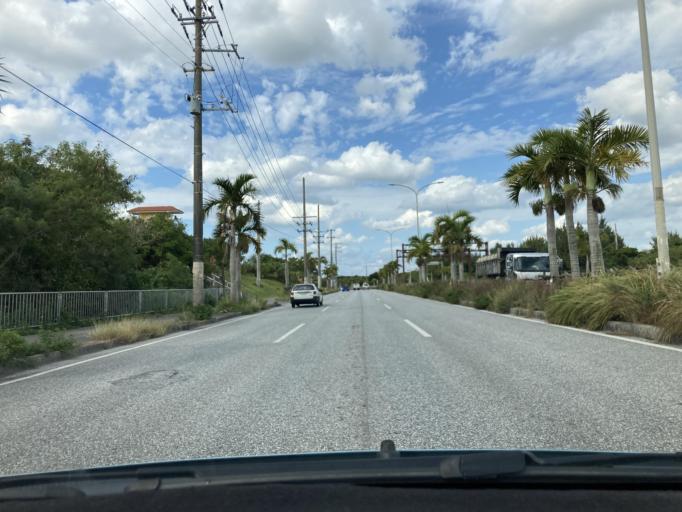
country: JP
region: Okinawa
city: Chatan
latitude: 26.3486
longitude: 127.7468
